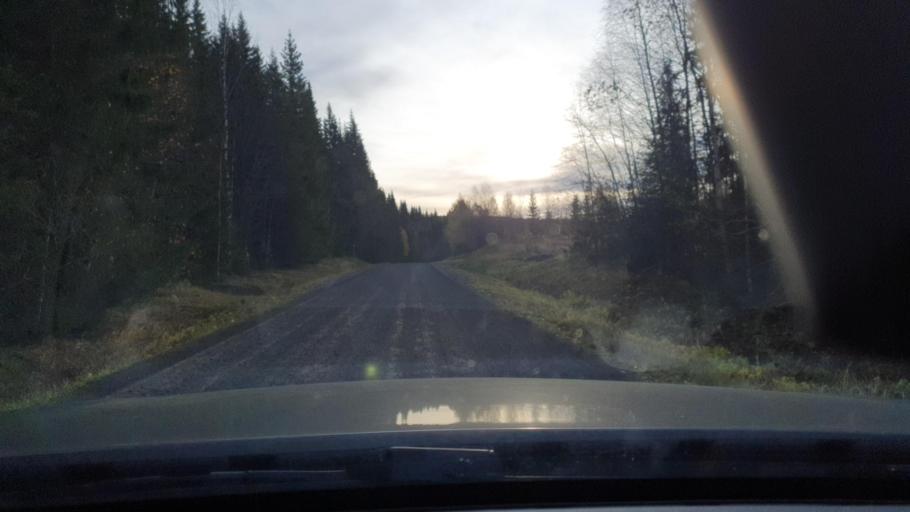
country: SE
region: Jaemtland
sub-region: Stroemsunds Kommun
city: Stroemsund
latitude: 63.5151
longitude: 15.6503
